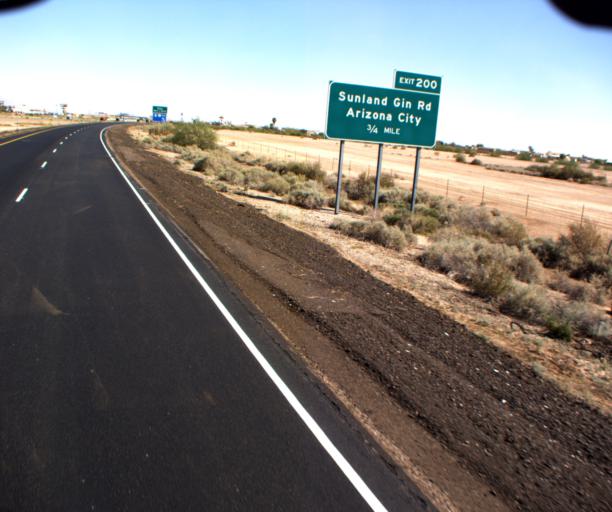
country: US
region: Arizona
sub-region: Pinal County
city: Arizona City
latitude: 32.8176
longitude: -111.6841
